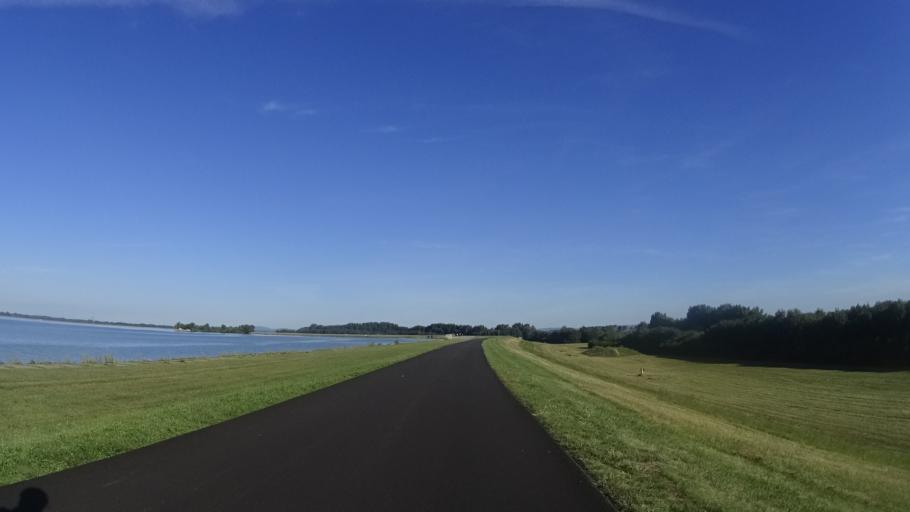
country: SK
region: Trnavsky
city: Samorin
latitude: 48.0163
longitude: 17.2939
